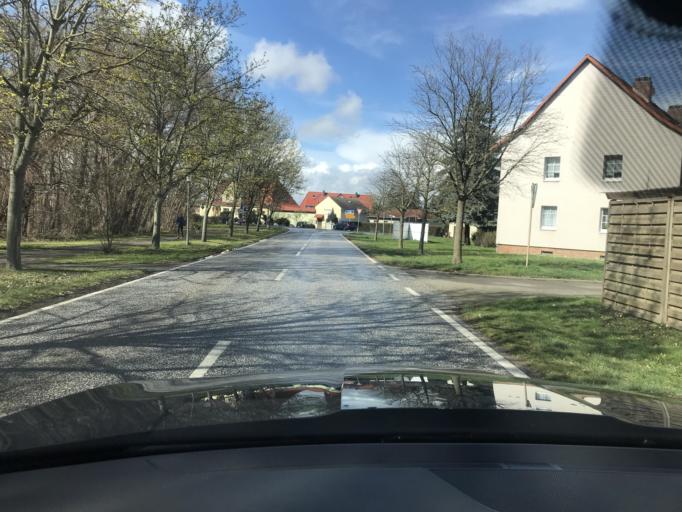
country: DE
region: Saxony-Anhalt
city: Hoym
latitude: 51.7857
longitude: 11.3198
